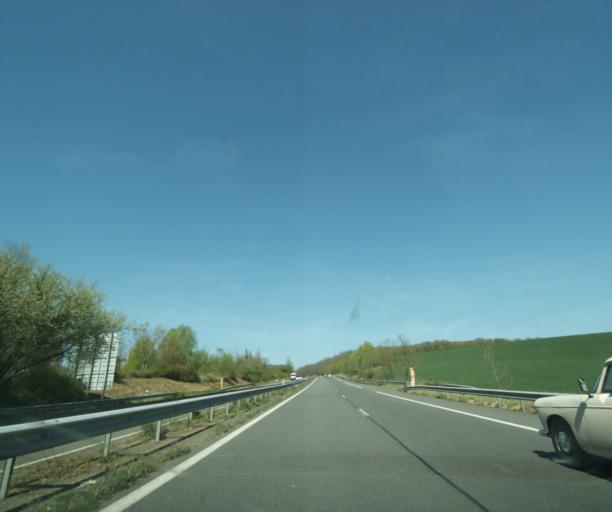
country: FR
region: Bourgogne
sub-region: Departement de la Nievre
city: Chaulgnes
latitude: 47.1067
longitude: 3.0706
